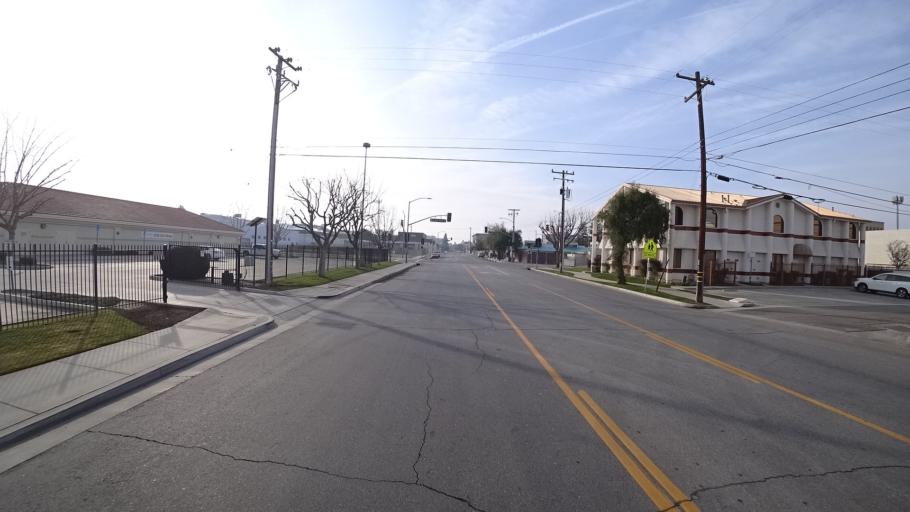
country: US
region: California
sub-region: Kern County
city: Bakersfield
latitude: 35.3787
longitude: -119.0152
